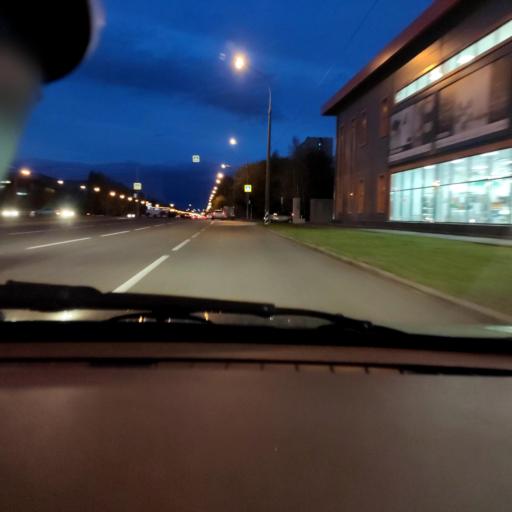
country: RU
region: Samara
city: Tol'yatti
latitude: 53.5014
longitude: 49.2756
